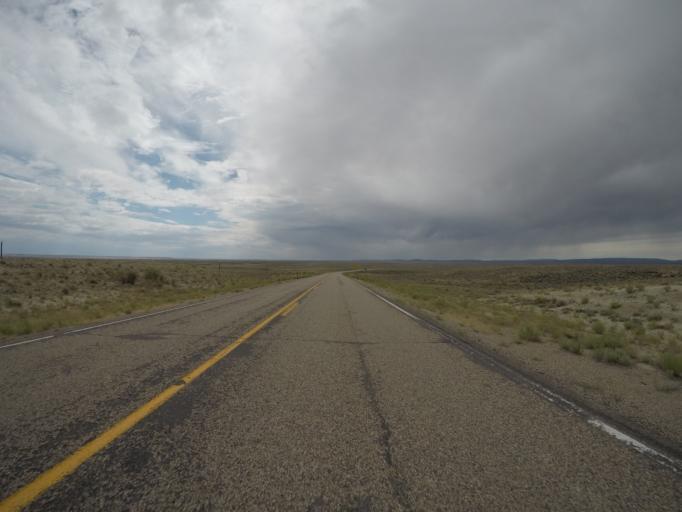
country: US
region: Wyoming
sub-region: Lincoln County
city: Kemmerer
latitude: 41.9644
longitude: -110.0968
